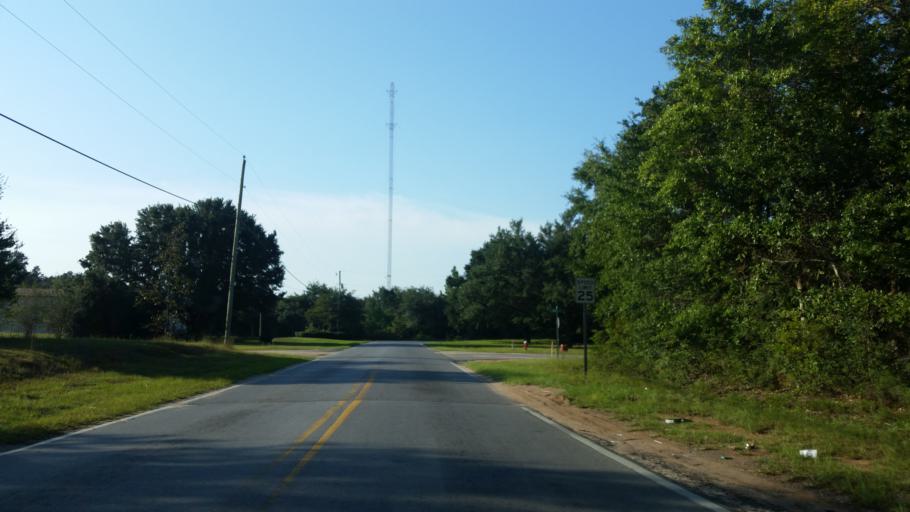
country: US
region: Florida
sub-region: Santa Rosa County
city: Bagdad
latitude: 30.5878
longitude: -87.0748
